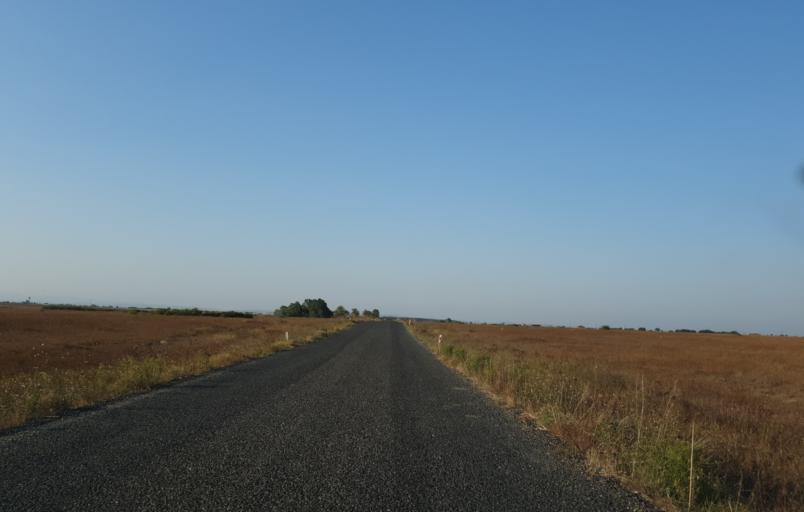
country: TR
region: Tekirdag
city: Beyazkoy
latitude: 41.4111
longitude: 27.7620
